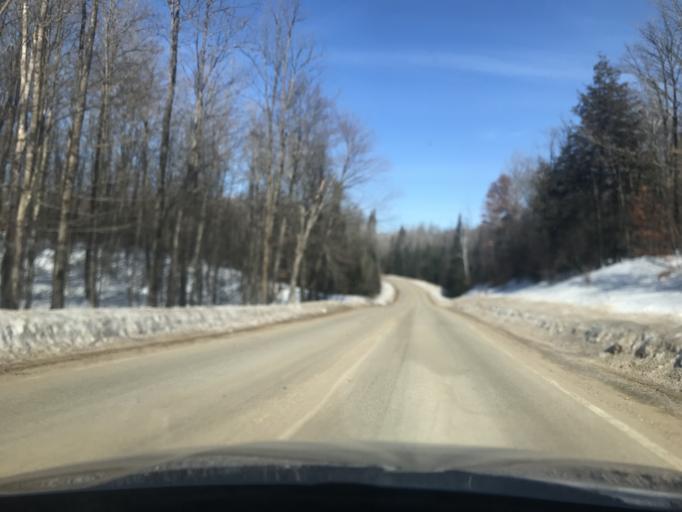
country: US
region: Michigan
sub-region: Dickinson County
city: Kingsford
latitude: 45.4101
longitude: -88.3899
